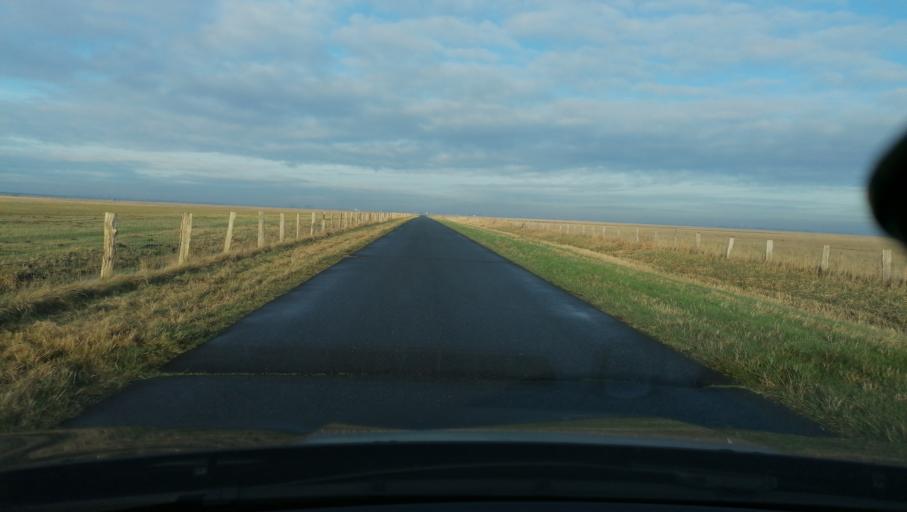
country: DE
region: Schleswig-Holstein
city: Friedrichsgabekoog
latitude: 54.1058
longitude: 8.9535
